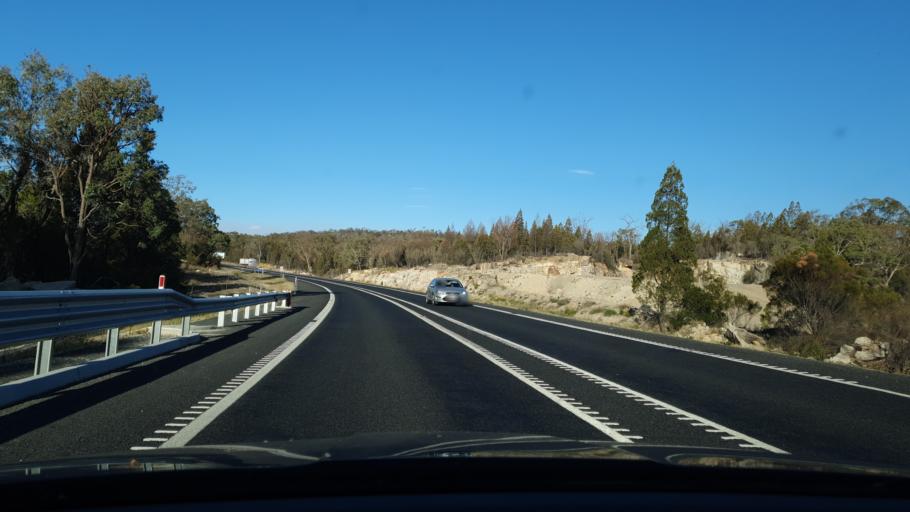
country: AU
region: Queensland
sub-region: Southern Downs
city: Stanthorpe
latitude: -28.6837
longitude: 151.9169
